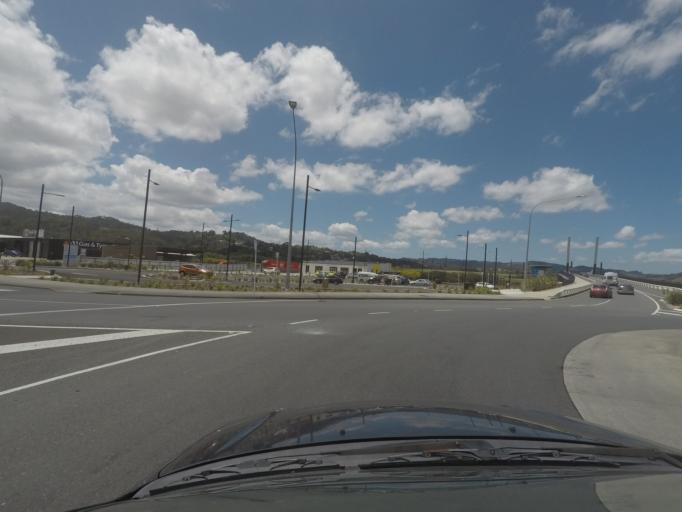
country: NZ
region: Northland
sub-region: Whangarei
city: Whangarei
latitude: -35.7351
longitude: 174.3328
